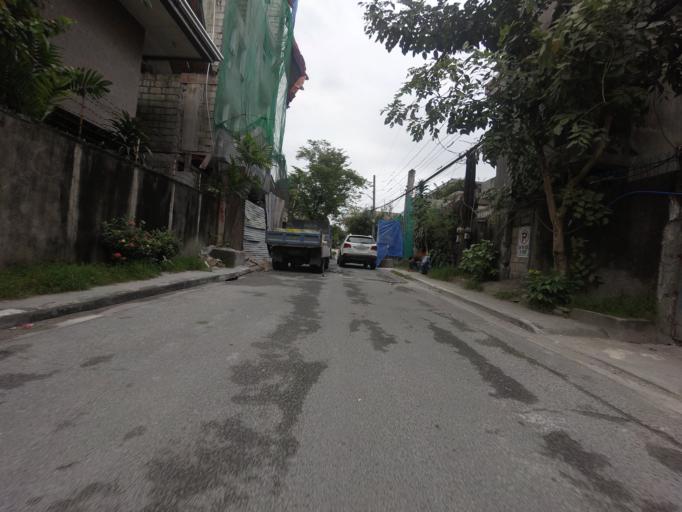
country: PH
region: Metro Manila
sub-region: San Juan
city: San Juan
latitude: 14.5946
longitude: 121.0414
